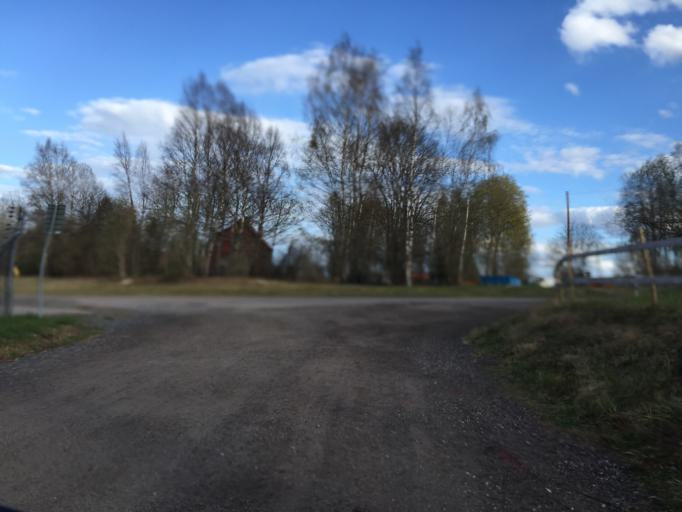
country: SE
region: Dalarna
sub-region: Ludvika Kommun
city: Ludvika
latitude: 60.1236
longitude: 15.1772
